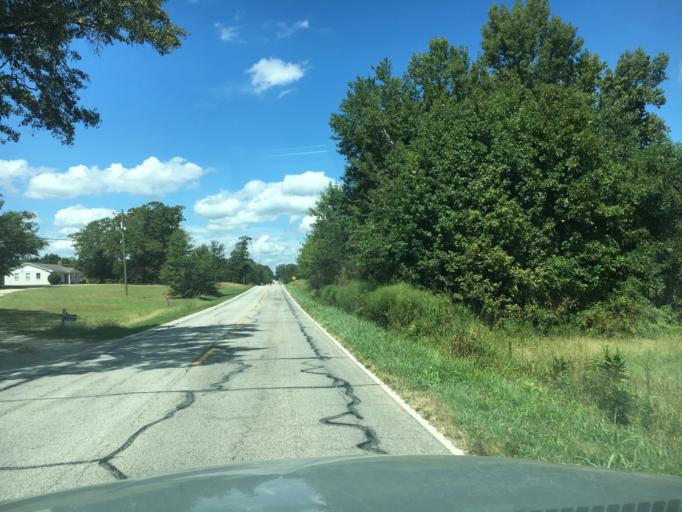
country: US
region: South Carolina
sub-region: Laurens County
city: Laurens
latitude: 34.5105
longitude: -82.0860
